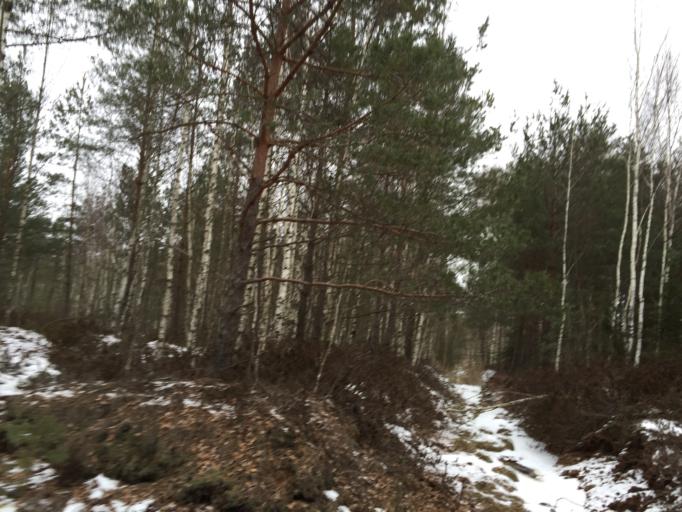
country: LV
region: Saulkrastu
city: Saulkrasti
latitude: 57.2376
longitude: 24.5060
